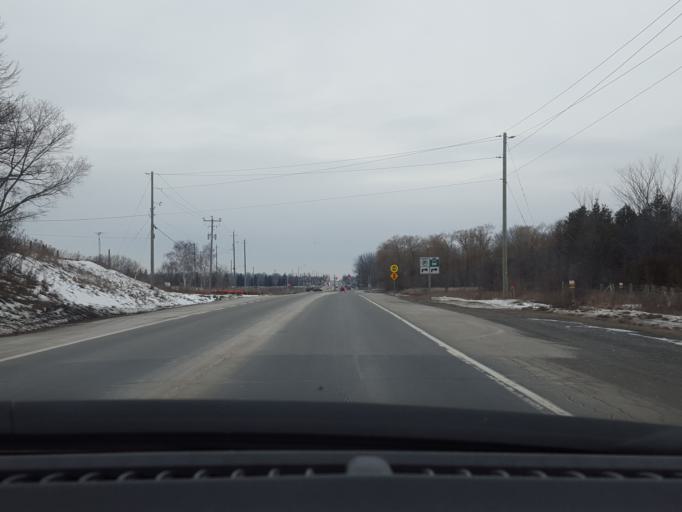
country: CA
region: Ontario
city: Keswick
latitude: 44.1877
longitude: -79.4369
